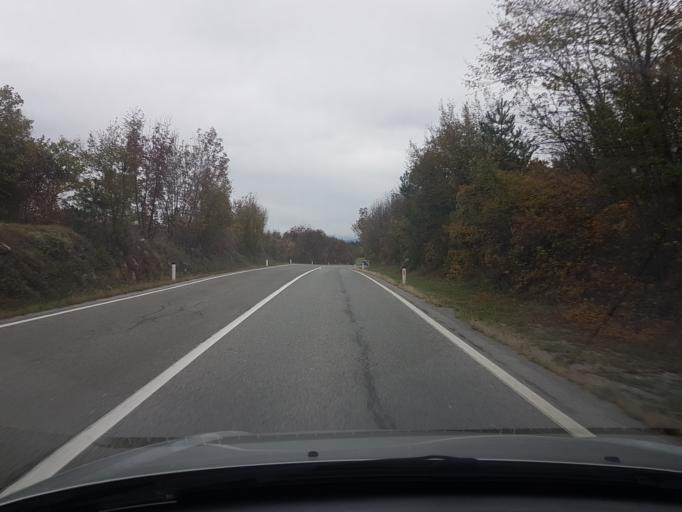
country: SI
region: Sezana
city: Sezana
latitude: 45.7183
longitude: 13.8935
